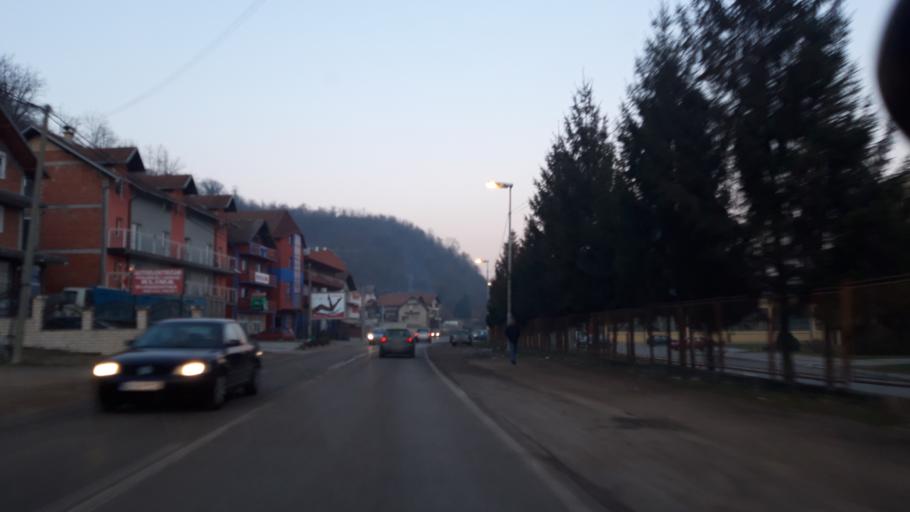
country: BA
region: Republika Srpska
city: Zvornik
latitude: 44.4043
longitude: 19.1176
